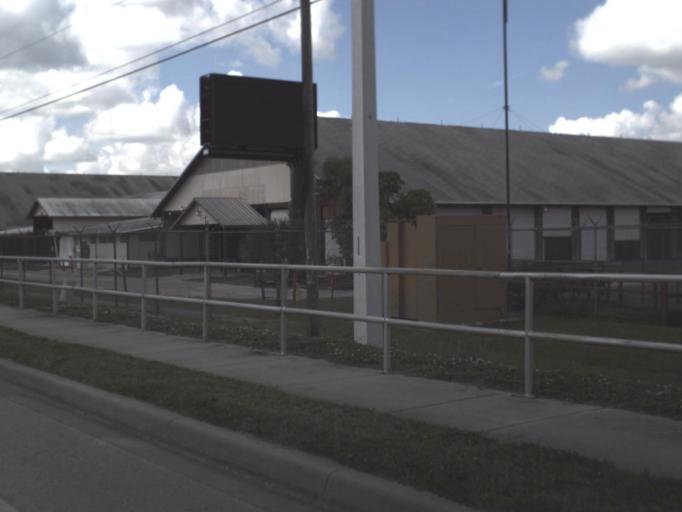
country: US
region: Florida
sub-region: Lee County
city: Fort Myers
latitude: 26.6415
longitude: -81.8264
